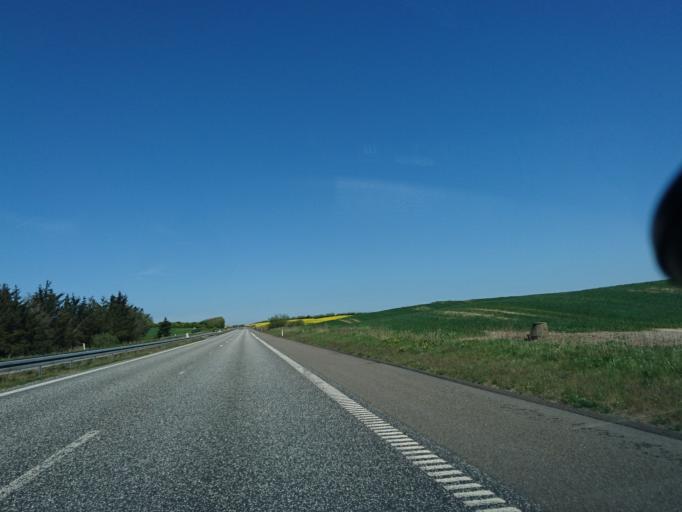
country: DK
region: North Denmark
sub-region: Hjorring Kommune
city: Hirtshals
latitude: 57.5518
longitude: 10.0093
